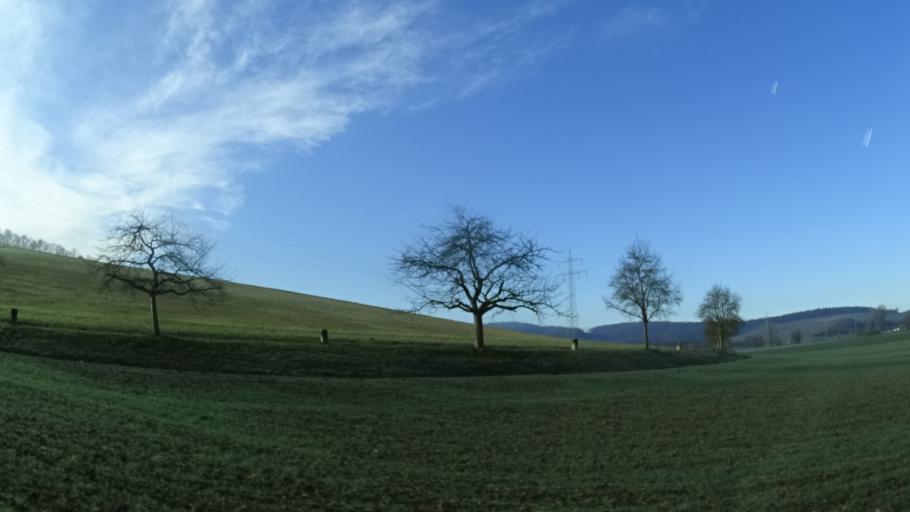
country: DE
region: Bavaria
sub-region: Regierungsbezirk Unterfranken
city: Waldbrunn
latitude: 49.7718
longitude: 9.7862
